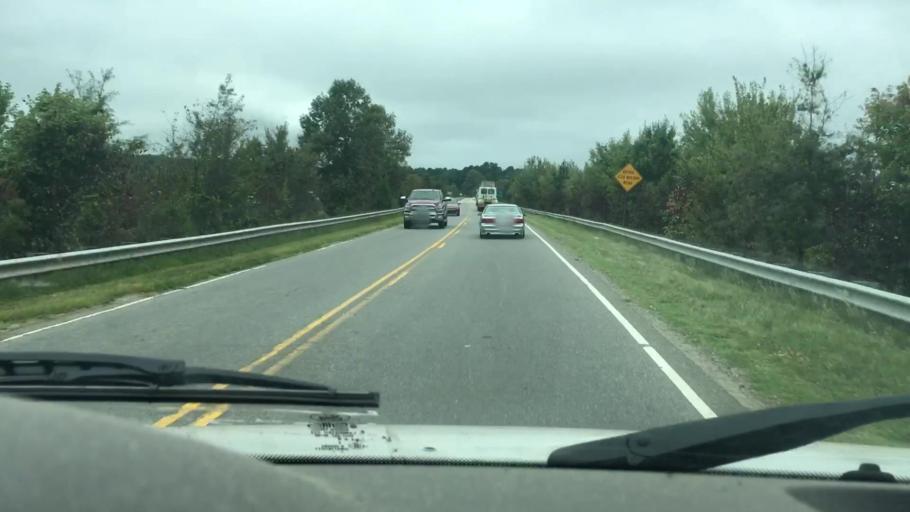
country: US
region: North Carolina
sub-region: Catawba County
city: Lake Norman of Catawba
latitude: 35.6057
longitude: -80.9395
